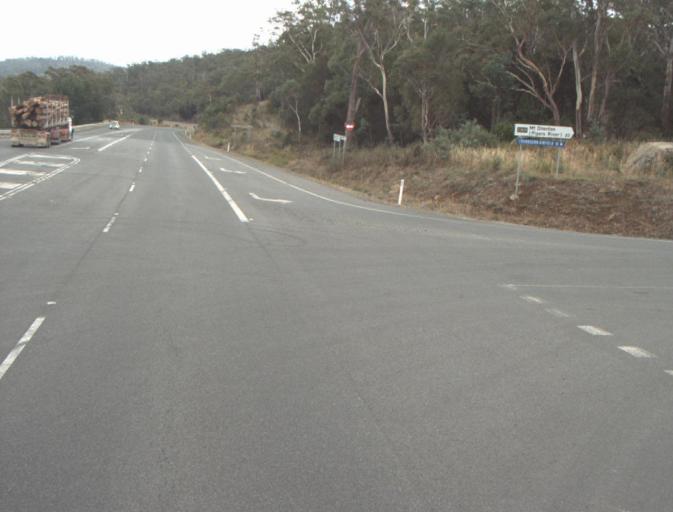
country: AU
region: Tasmania
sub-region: Launceston
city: Mayfield
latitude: -41.2433
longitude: 147.0165
